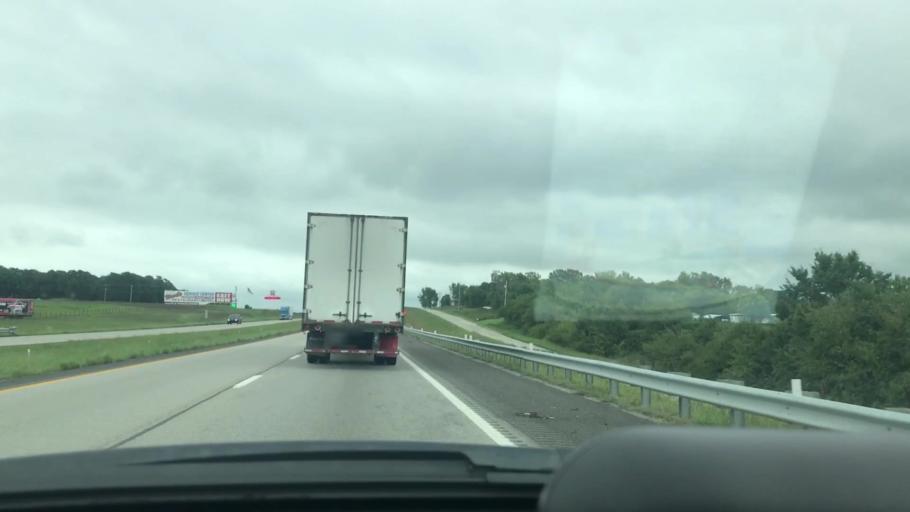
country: US
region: Missouri
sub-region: Greene County
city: Republic
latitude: 37.1841
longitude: -93.5795
